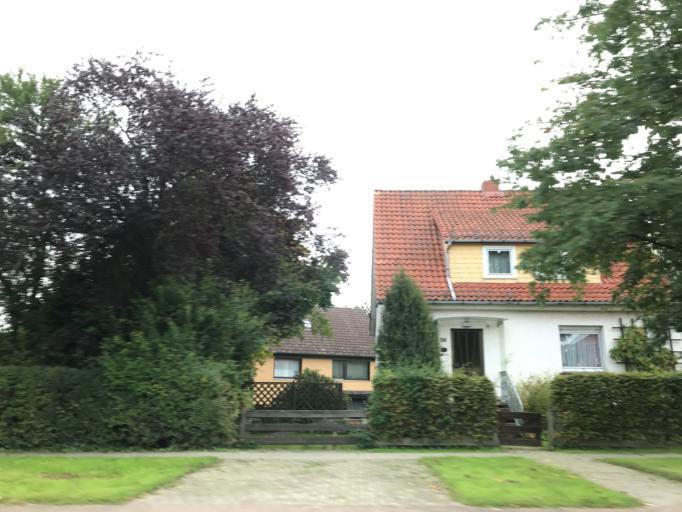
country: DE
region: Lower Saxony
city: Herzberg am Harz
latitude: 51.6587
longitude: 10.3504
